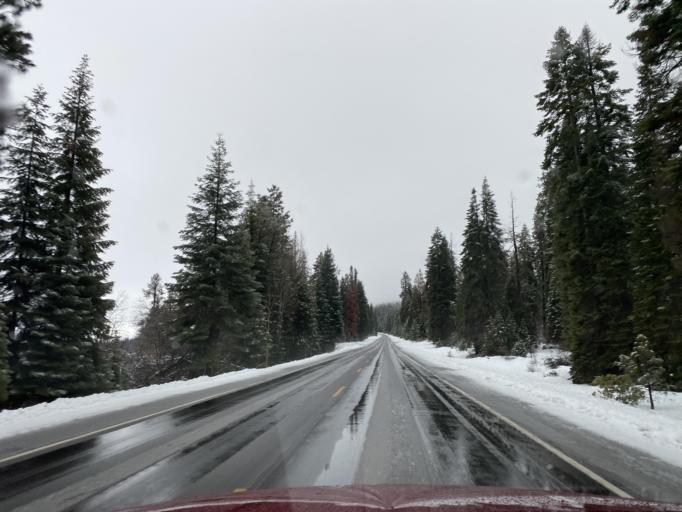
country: US
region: Oregon
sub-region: Klamath County
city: Klamath Falls
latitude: 42.5462
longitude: -122.0871
